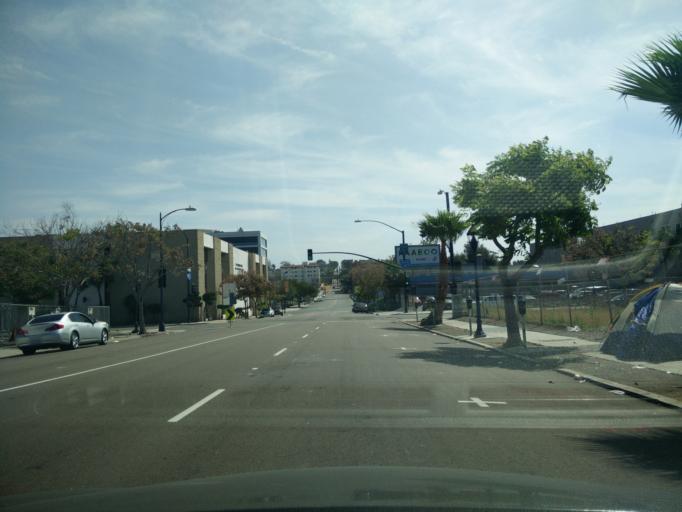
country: US
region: California
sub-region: San Diego County
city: San Diego
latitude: 32.7147
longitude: -117.1535
